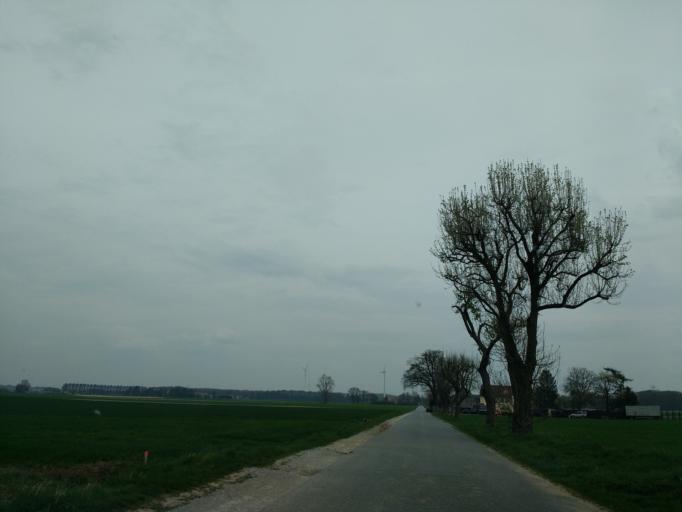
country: DE
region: North Rhine-Westphalia
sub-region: Regierungsbezirk Detmold
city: Salzkotten
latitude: 51.6883
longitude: 8.6279
